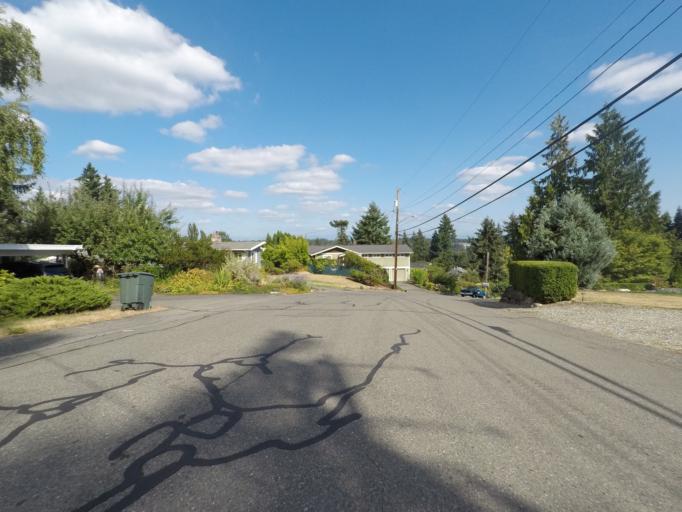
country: US
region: Washington
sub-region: King County
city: Kenmore
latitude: 47.7707
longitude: -122.2534
